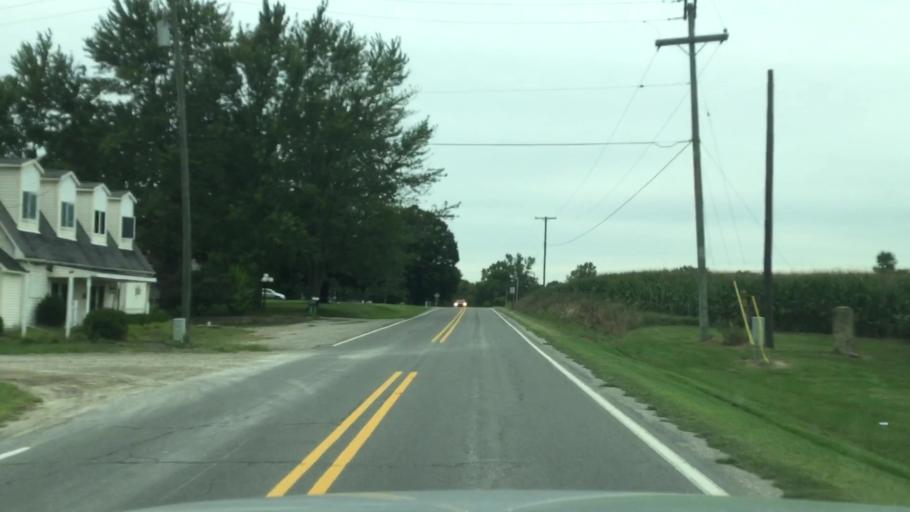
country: US
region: Michigan
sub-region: Washtenaw County
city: Milan
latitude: 42.1502
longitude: -83.6534
